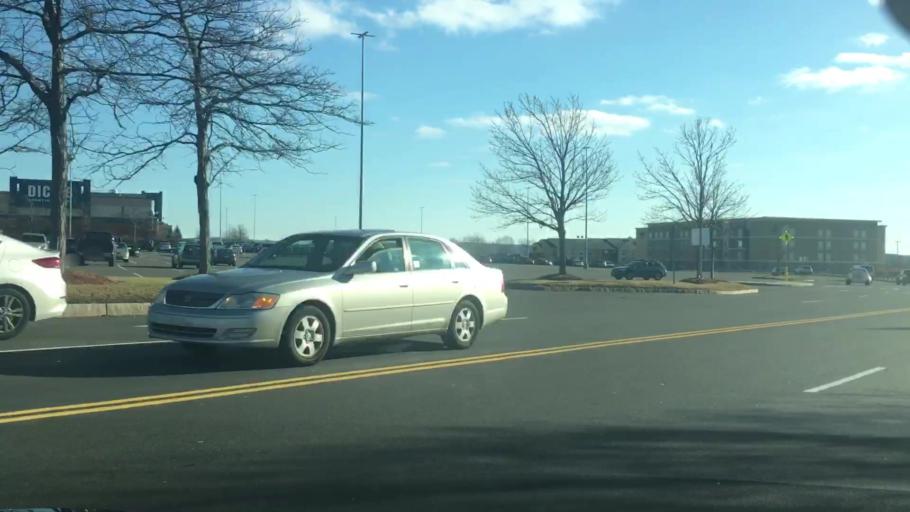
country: US
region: Connecticut
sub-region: Hartford County
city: Manchester
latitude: 41.8074
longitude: -72.5494
